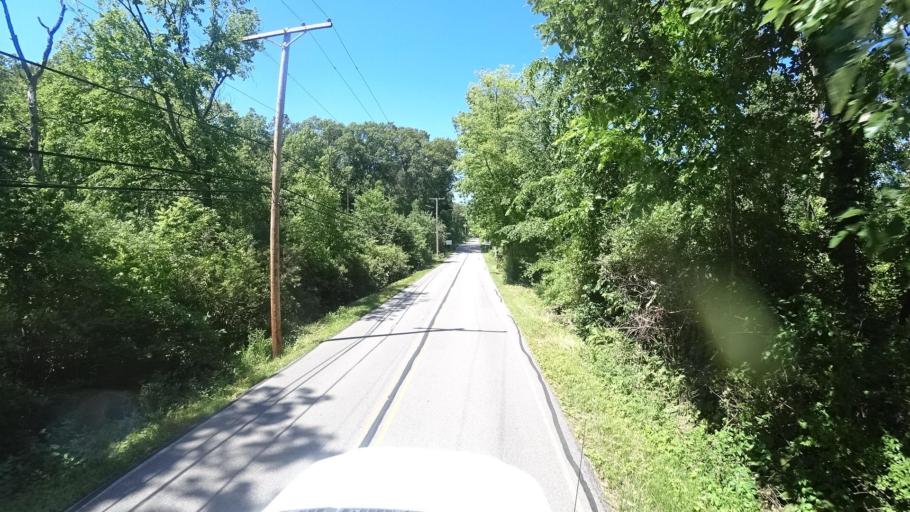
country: US
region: Indiana
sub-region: Porter County
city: Porter
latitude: 41.6517
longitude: -87.0674
